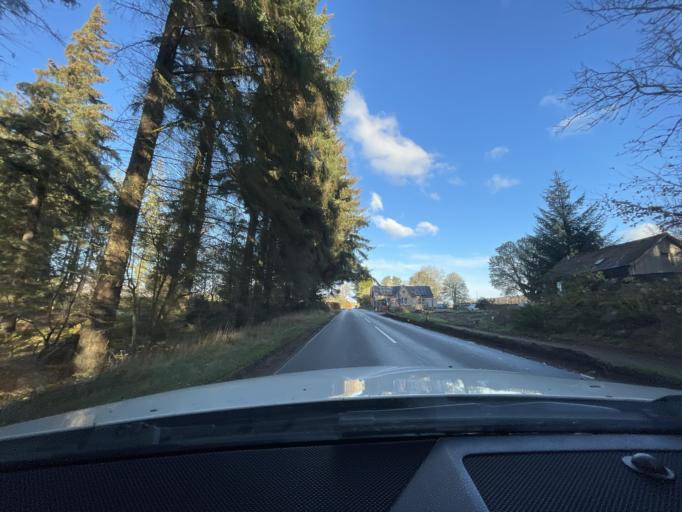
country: GB
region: Scotland
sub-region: Highland
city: Inverness
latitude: 57.3955
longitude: -4.3208
